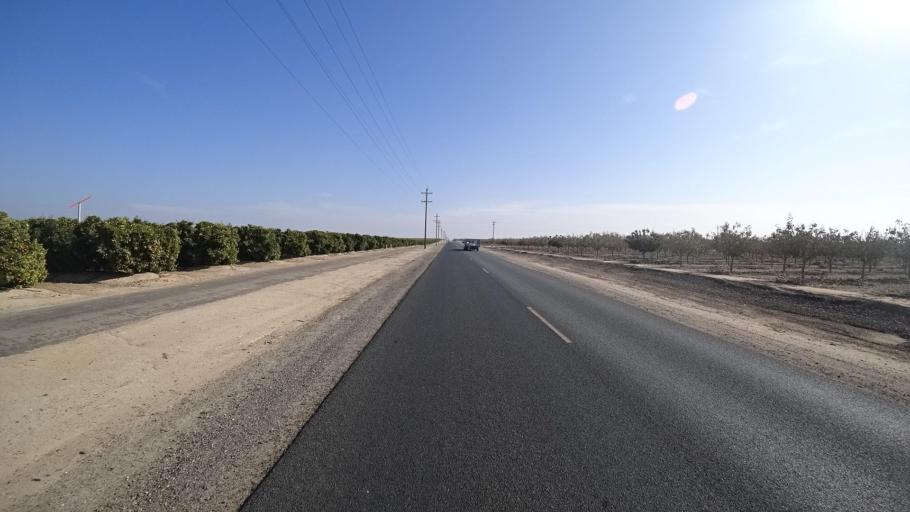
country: US
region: California
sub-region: Kern County
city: McFarland
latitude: 35.6021
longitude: -119.1793
